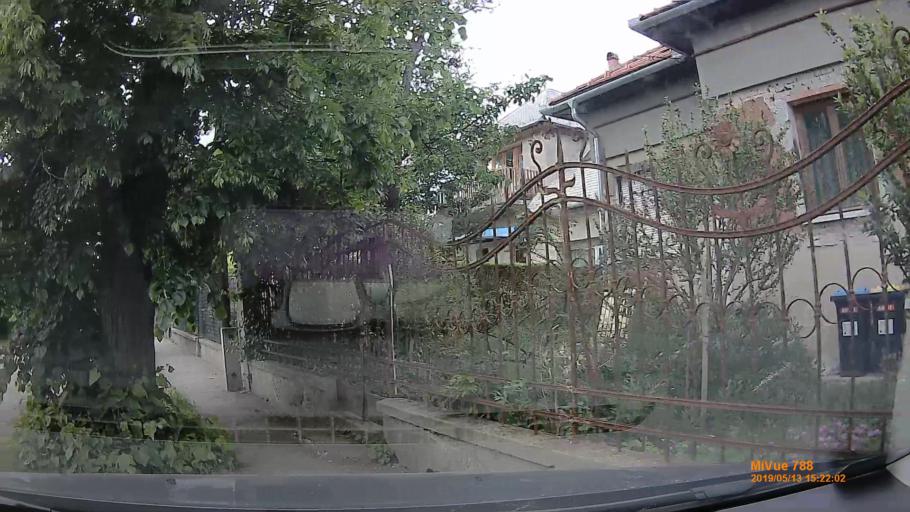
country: HU
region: Budapest
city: Budapest XVII. keruelet
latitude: 47.4931
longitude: 19.2570
